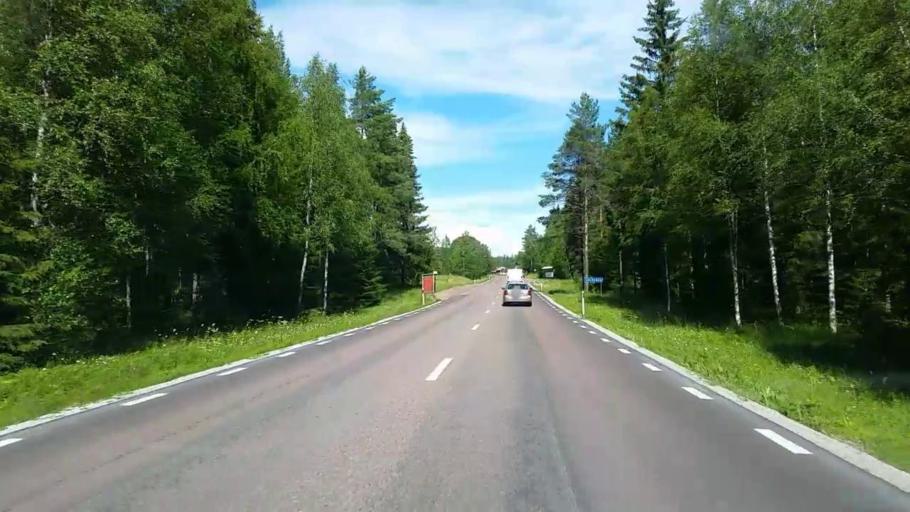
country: SE
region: Dalarna
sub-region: Rattviks Kommun
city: Raettvik
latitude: 60.9735
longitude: 15.2231
